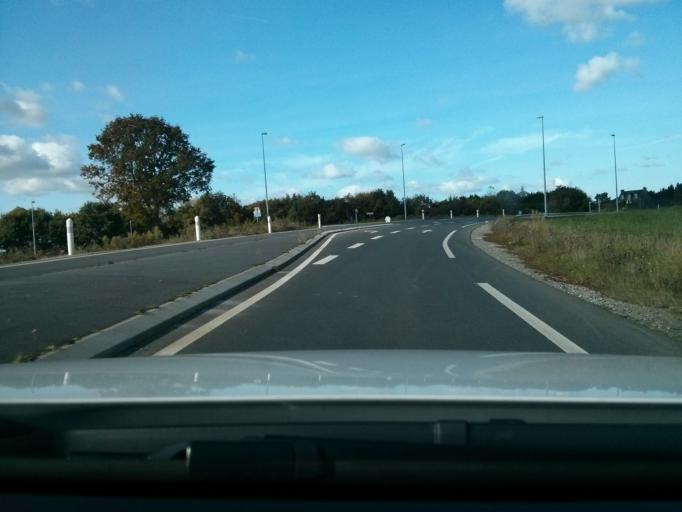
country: FR
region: Brittany
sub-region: Departement des Cotes-d'Armor
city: Pleslin-Trigavou
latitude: 48.5217
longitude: -2.0437
